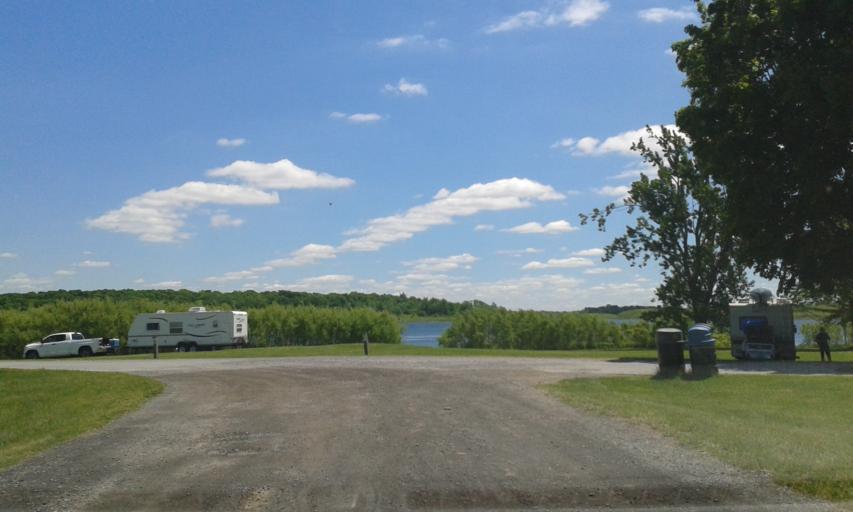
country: US
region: New York
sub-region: St. Lawrence County
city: Massena
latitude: 44.9991
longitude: -74.8986
